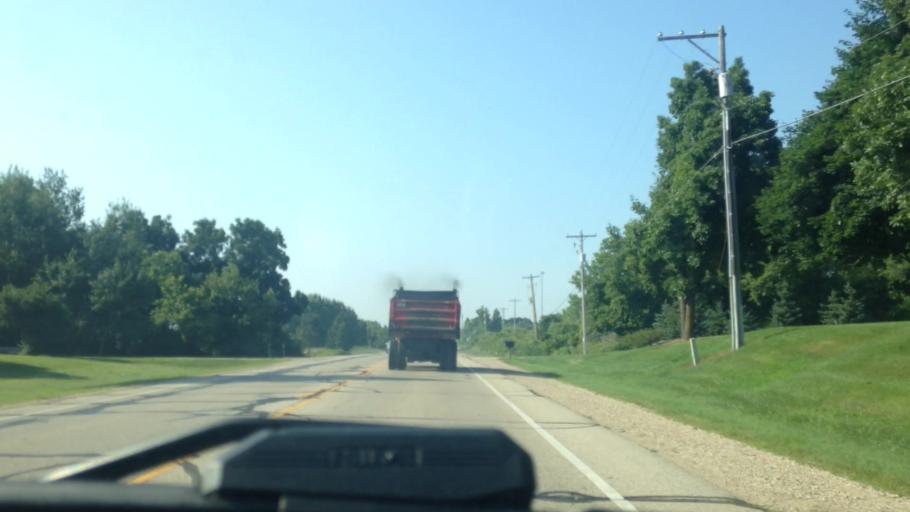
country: US
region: Wisconsin
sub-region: Waukesha County
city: Merton
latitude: 43.1714
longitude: -88.2625
